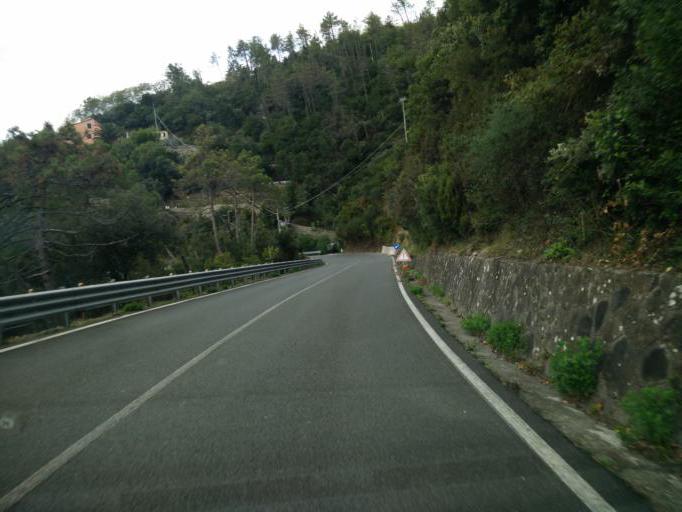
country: IT
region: Liguria
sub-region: Provincia di La Spezia
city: Riomaggiore
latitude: 44.0877
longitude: 9.7684
